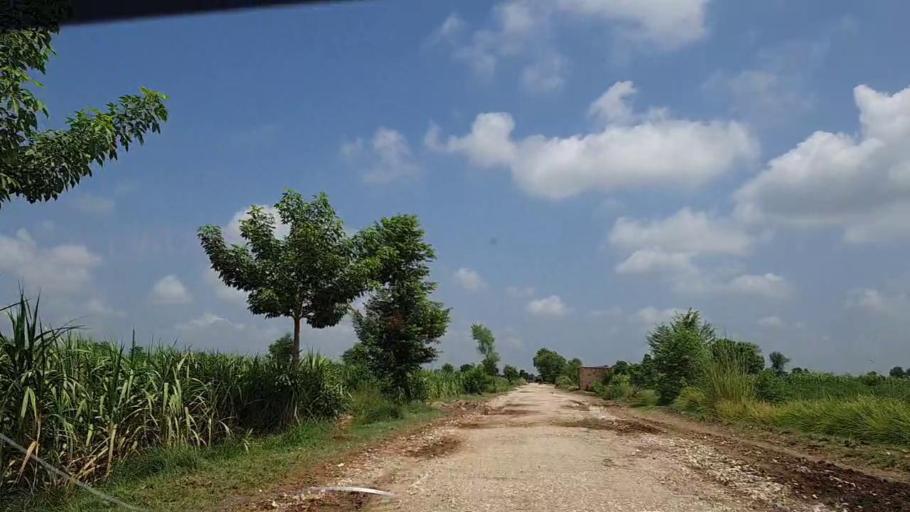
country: PK
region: Sindh
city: Tharu Shah
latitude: 26.9003
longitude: 68.0394
